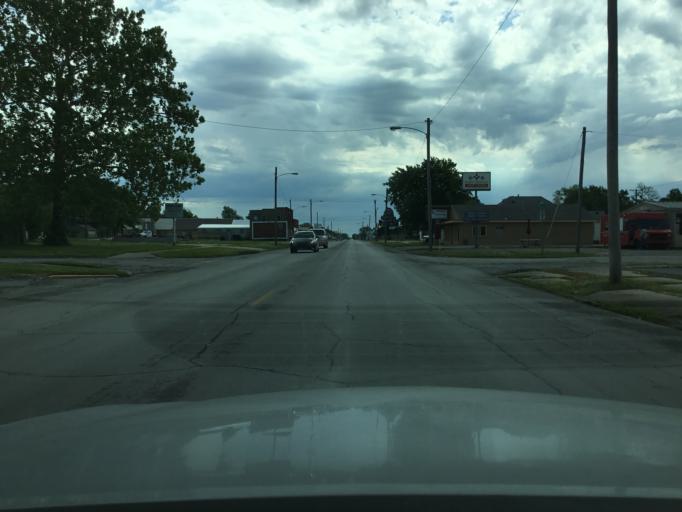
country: US
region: Kansas
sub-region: Montgomery County
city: Coffeyville
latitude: 37.0362
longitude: -95.6402
